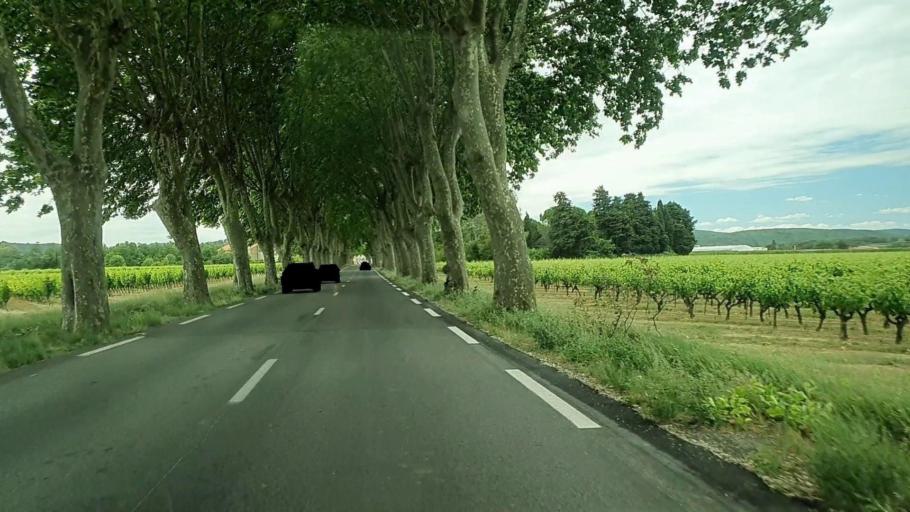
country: FR
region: Languedoc-Roussillon
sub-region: Departement du Gard
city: Connaux
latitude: 44.0984
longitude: 4.6019
